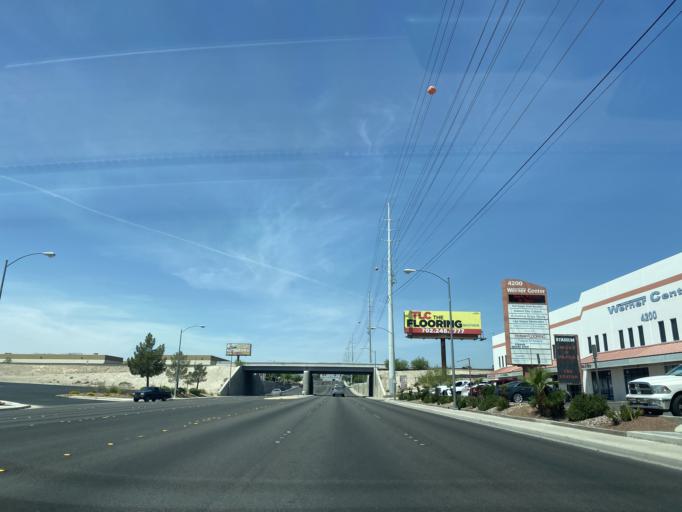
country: US
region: Nevada
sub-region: Clark County
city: Paradise
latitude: 36.0864
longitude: -115.1958
